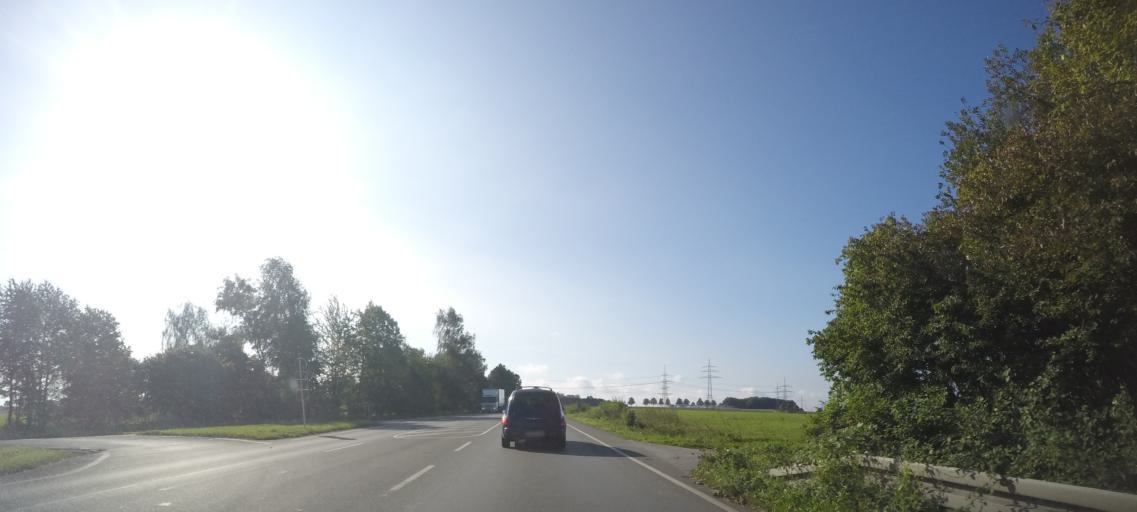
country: DE
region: North Rhine-Westphalia
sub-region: Regierungsbezirk Arnsberg
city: Unna
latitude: 51.5068
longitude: 7.7016
